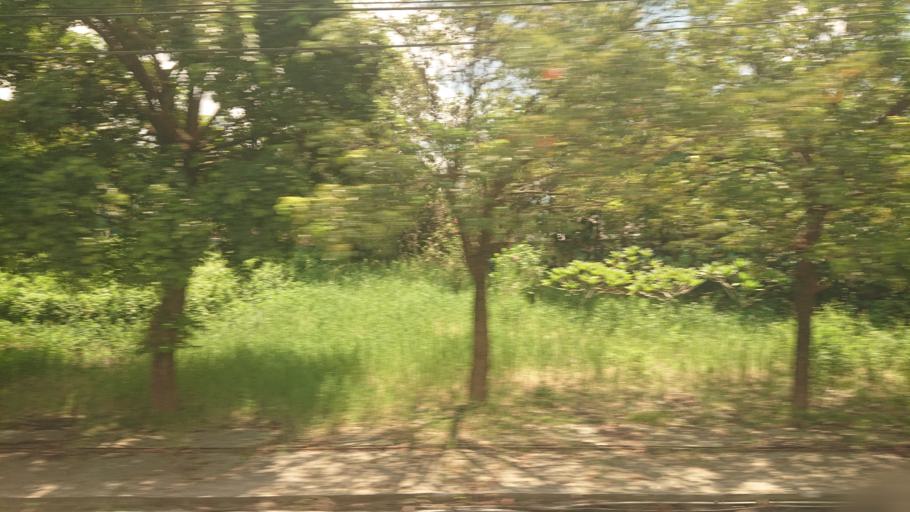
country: TW
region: Taiwan
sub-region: Nantou
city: Puli
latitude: 23.9863
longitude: 120.9586
